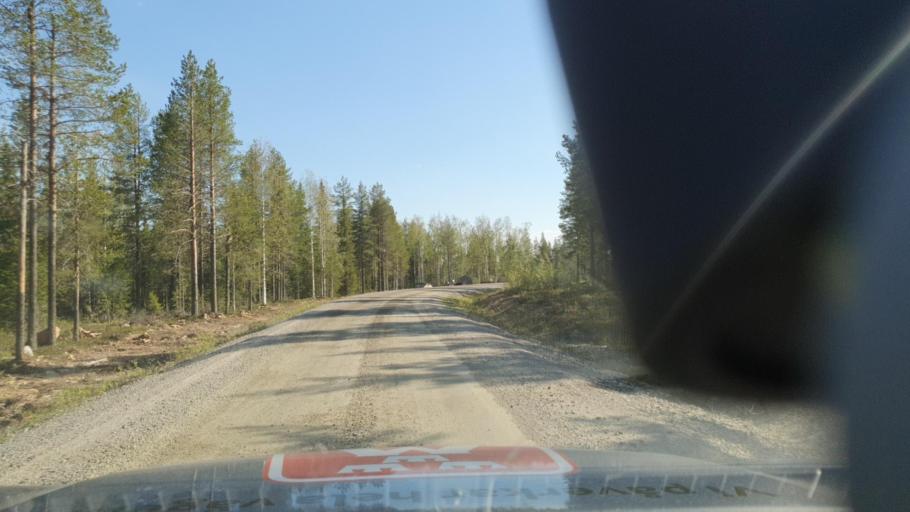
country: SE
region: Norrbotten
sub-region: Bodens Kommun
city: Boden
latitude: 66.4560
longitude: 21.8666
